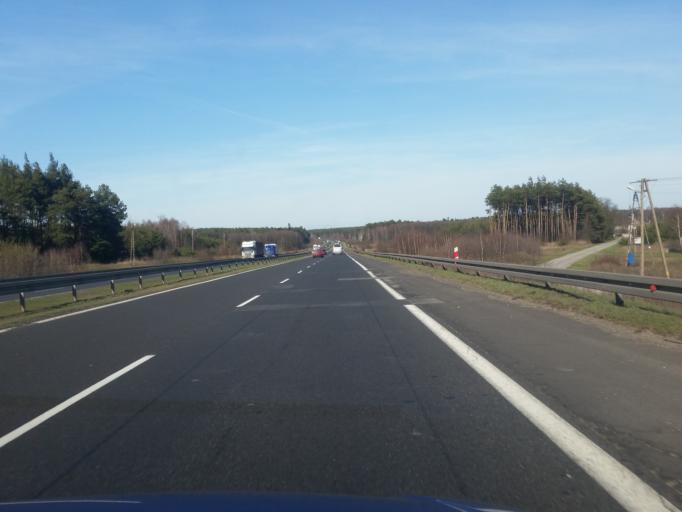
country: PL
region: Lodz Voivodeship
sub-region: Powiat radomszczanski
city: Gomunice
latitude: 51.1516
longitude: 19.4399
